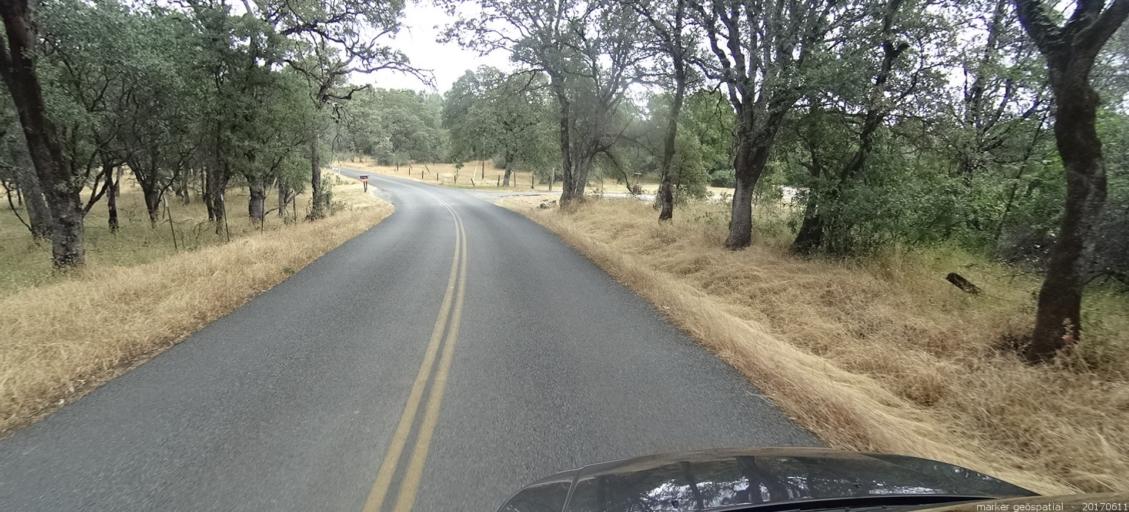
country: US
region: California
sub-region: Butte County
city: Oroville
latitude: 39.6107
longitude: -121.5276
